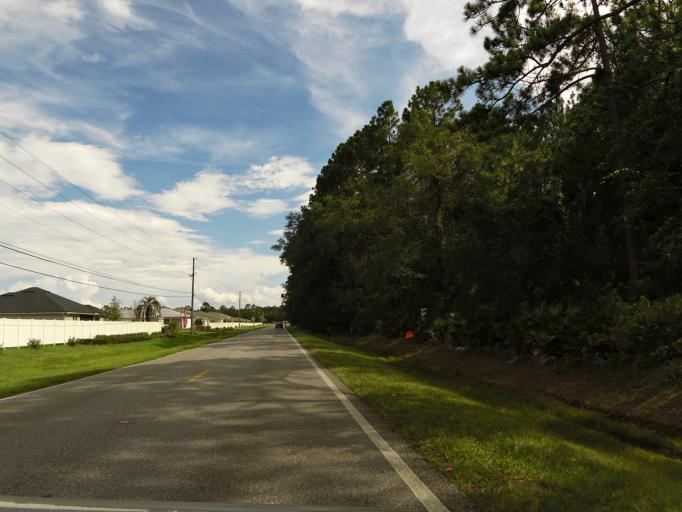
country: US
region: Florida
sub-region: Clay County
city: Green Cove Springs
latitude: 30.0263
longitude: -81.7191
